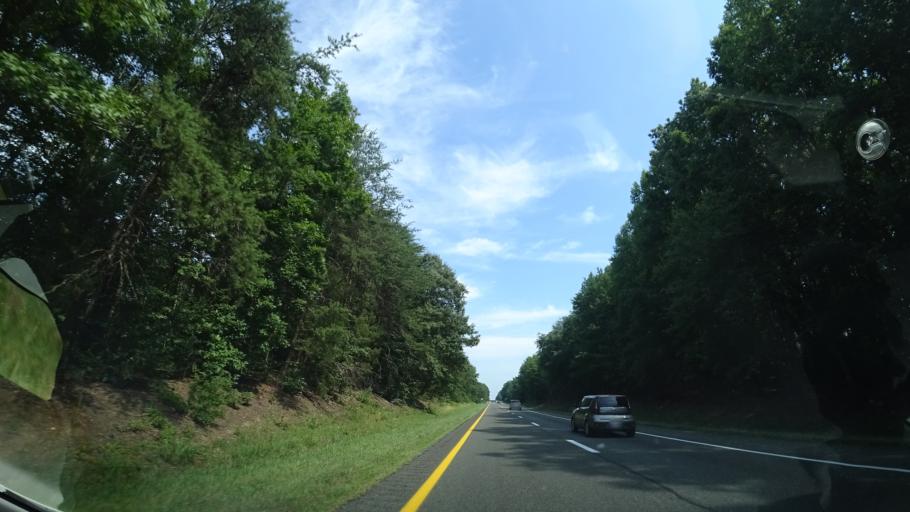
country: US
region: Virginia
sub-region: Louisa County
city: Louisa
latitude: 37.8514
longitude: -77.9902
